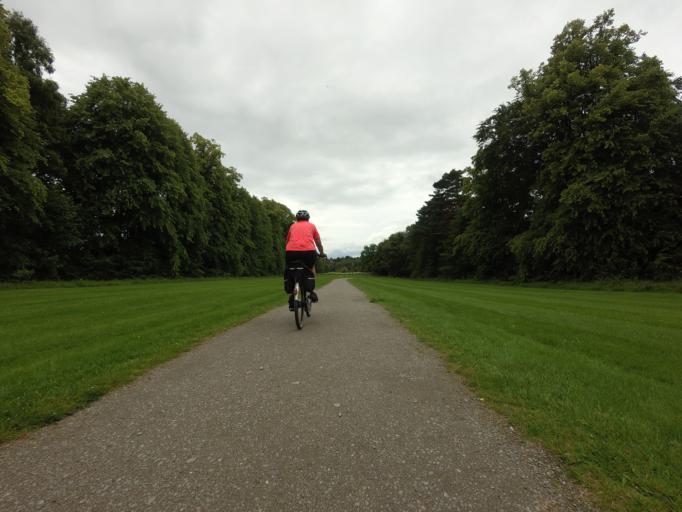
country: GB
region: Scotland
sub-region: Moray
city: Forres
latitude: 57.5967
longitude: -3.7125
